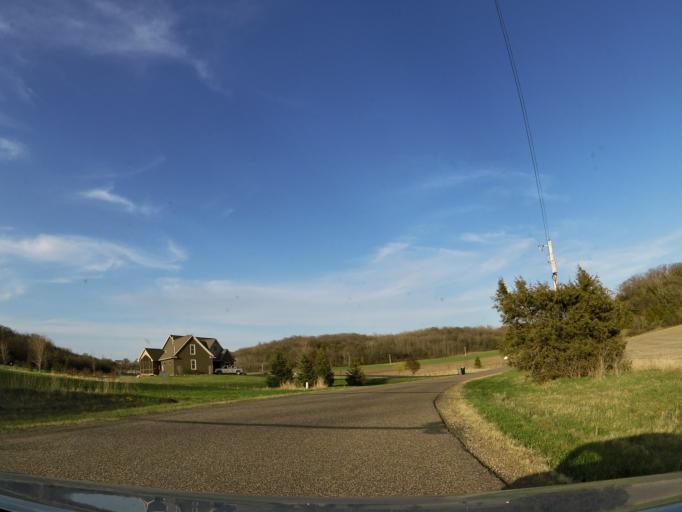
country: US
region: Wisconsin
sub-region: Pierce County
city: River Falls
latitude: 44.8869
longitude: -92.6737
